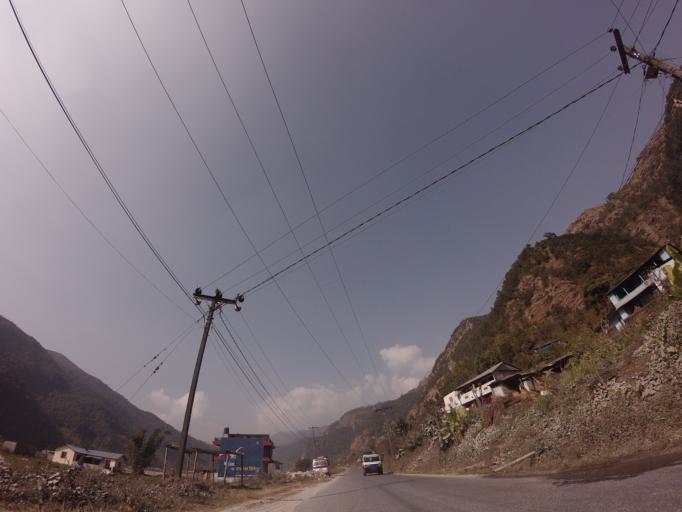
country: NP
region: Western Region
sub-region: Gandaki Zone
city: Pokhara
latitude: 28.2875
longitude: 83.8982
